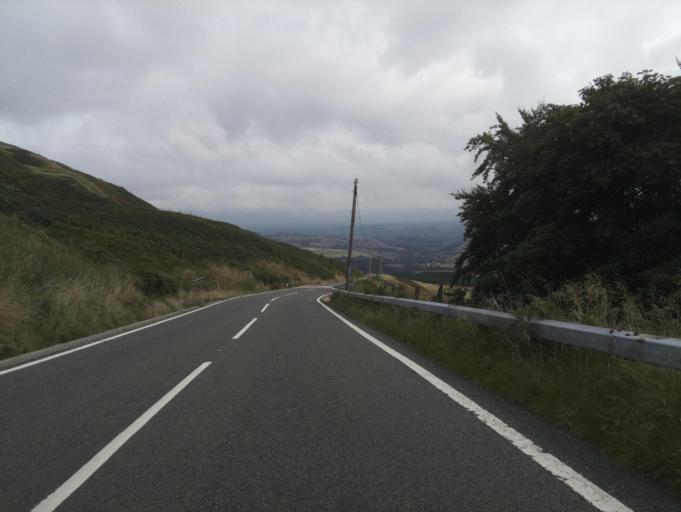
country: GB
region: England
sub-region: Kirklees
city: Meltham
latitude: 53.5356
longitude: -1.8537
